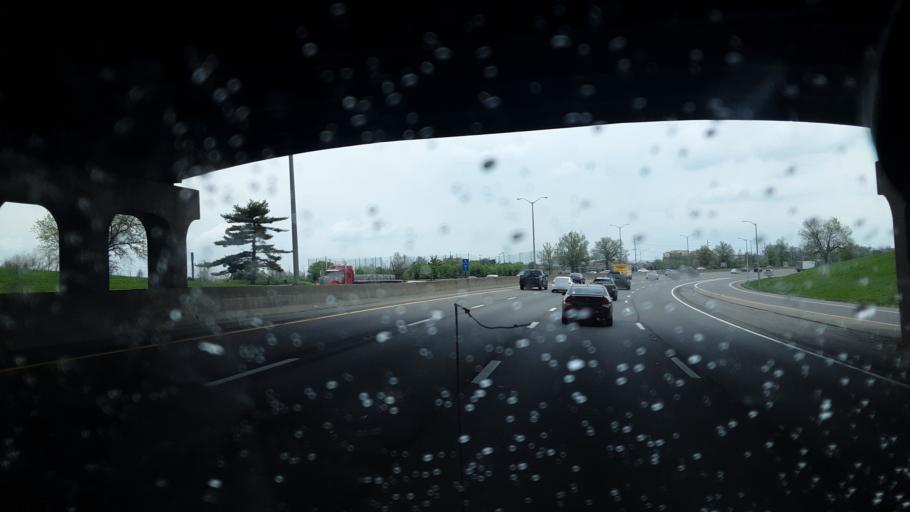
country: US
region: Kentucky
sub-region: Boone County
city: Florence
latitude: 39.0015
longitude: -84.6471
